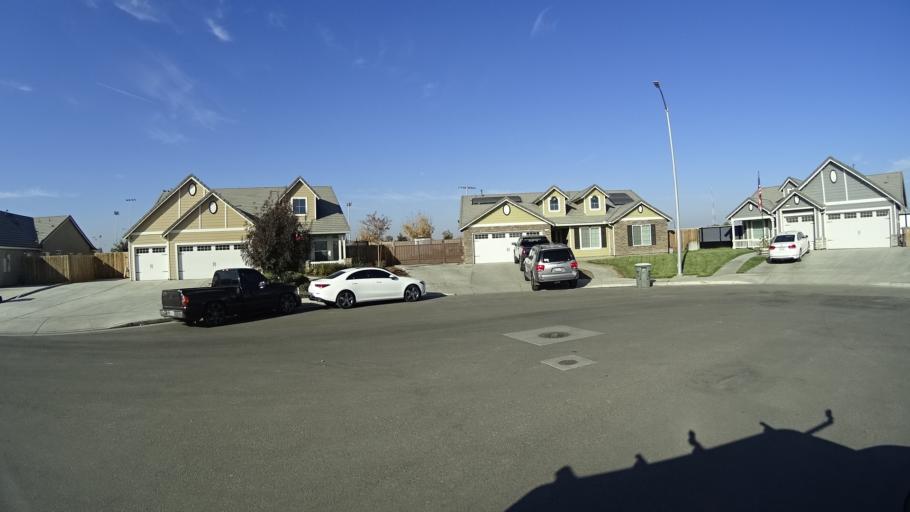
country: US
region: California
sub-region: Kern County
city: Greenfield
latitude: 35.2726
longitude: -119.0736
